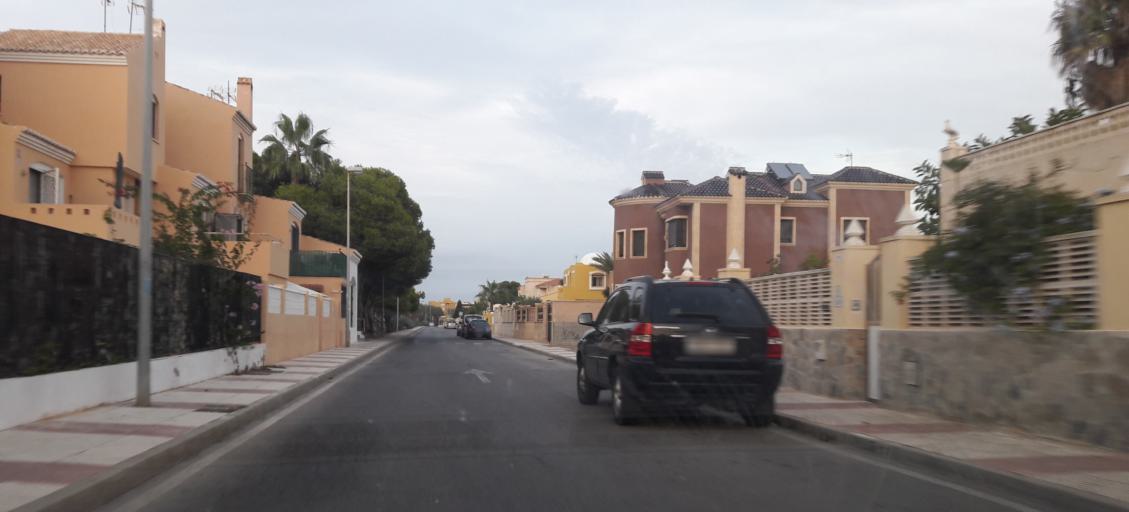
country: ES
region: Andalusia
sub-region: Provincia de Almeria
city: Roquetas de Mar
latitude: 36.7317
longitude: -2.6274
